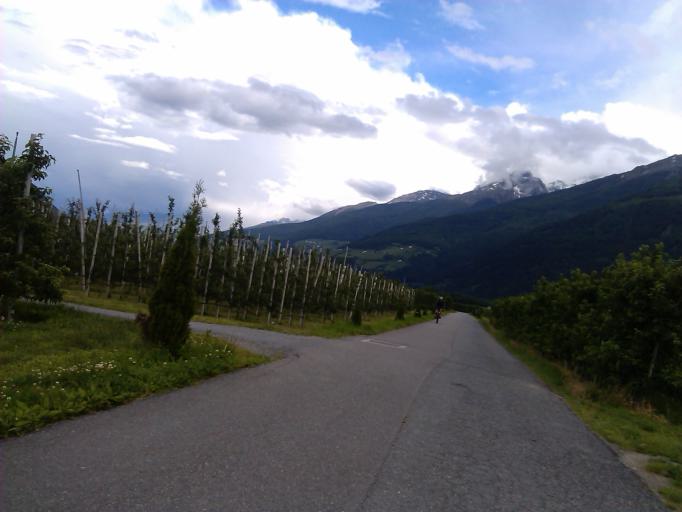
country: IT
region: Trentino-Alto Adige
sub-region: Bolzano
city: Prato Allo Stelvio
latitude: 46.6290
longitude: 10.6160
